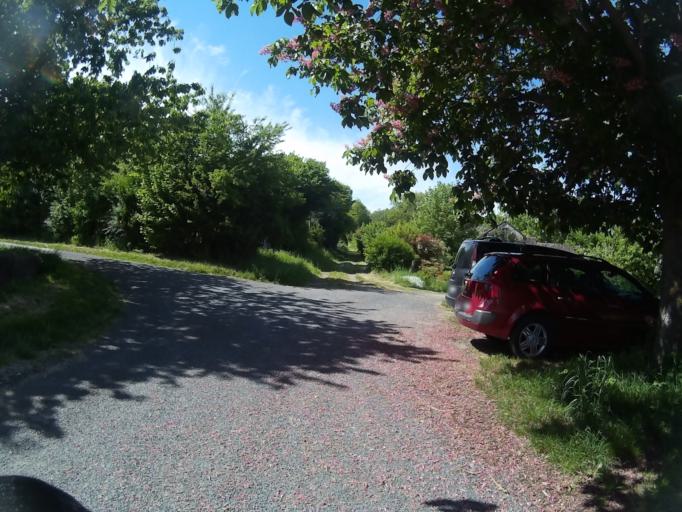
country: FR
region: Centre
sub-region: Departement du Loir-et-Cher
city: Lunay
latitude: 47.8140
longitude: 0.9536
